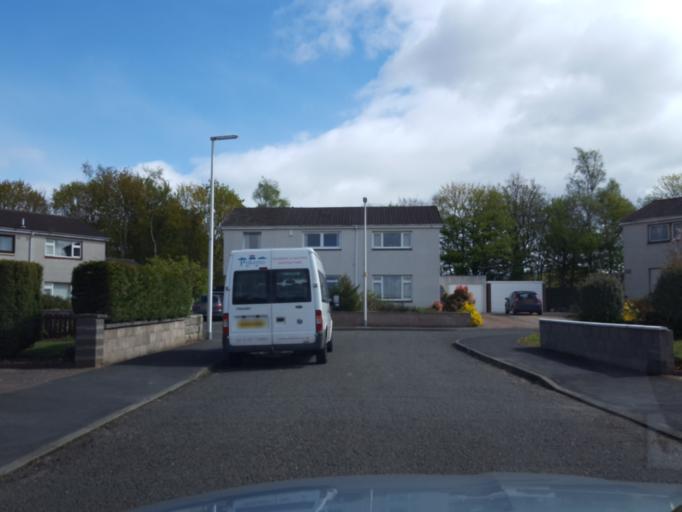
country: GB
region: Scotland
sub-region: Angus
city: Muirhead
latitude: 56.4706
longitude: -3.0526
